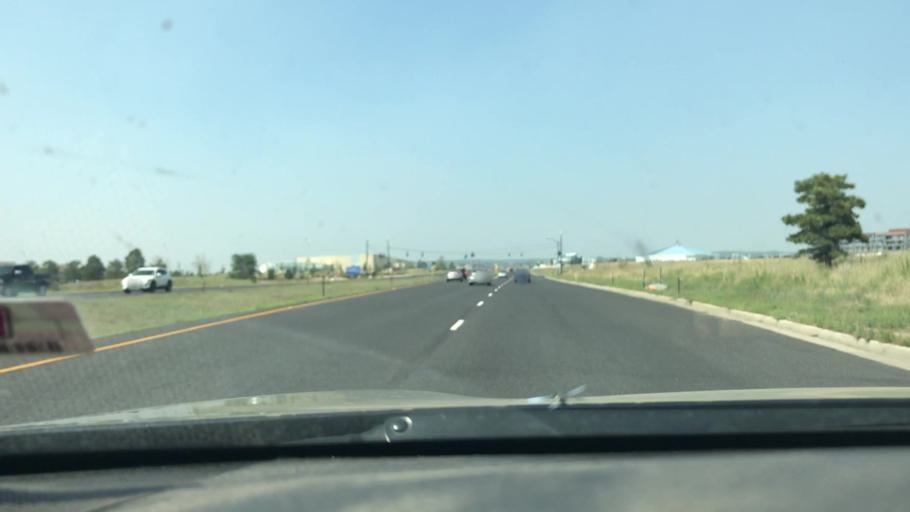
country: US
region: Colorado
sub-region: El Paso County
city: Air Force Academy
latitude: 38.9813
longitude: -104.7978
